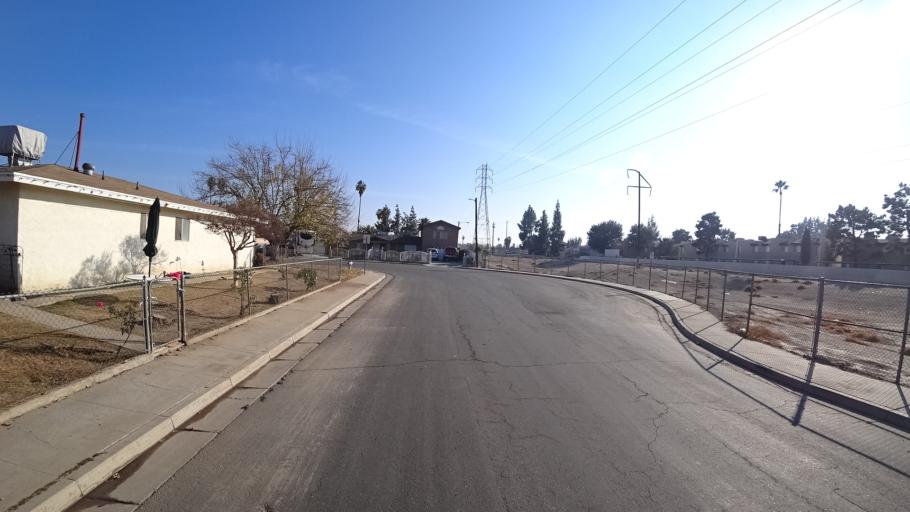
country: US
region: California
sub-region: Kern County
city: Greenfield
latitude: 35.3122
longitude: -119.0133
